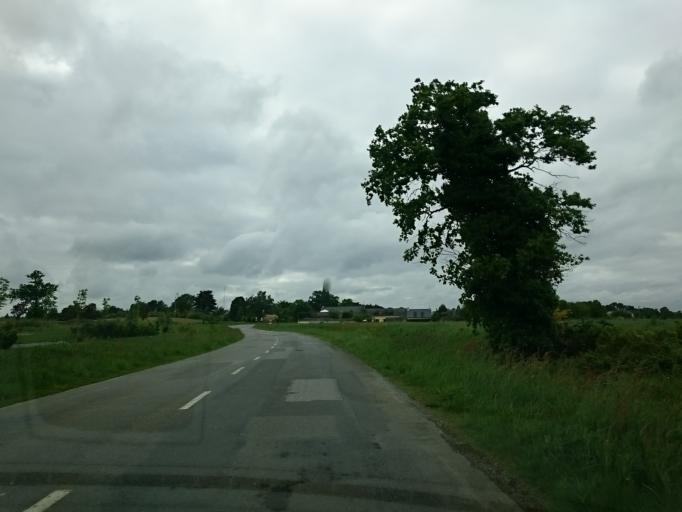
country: FR
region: Brittany
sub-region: Departement d'Ille-et-Vilaine
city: Chantepie
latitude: 48.0661
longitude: -1.6222
